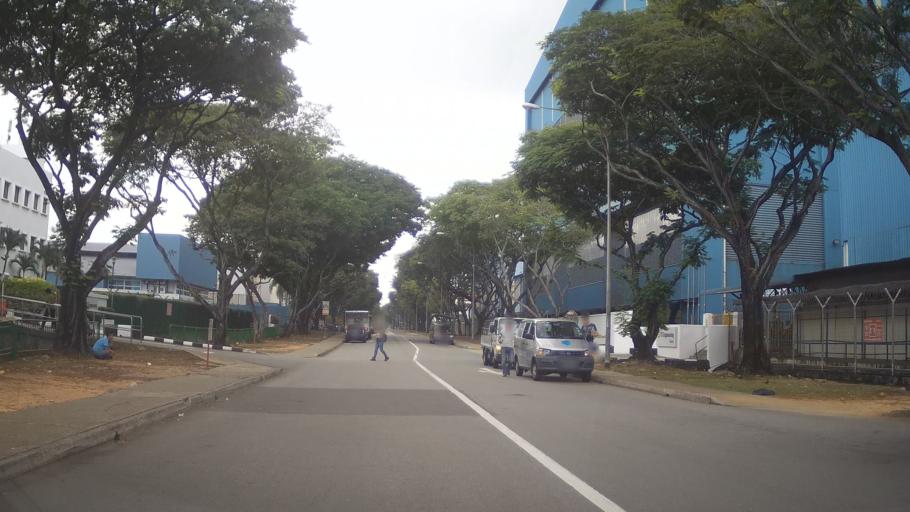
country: SG
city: Singapore
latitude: 1.3012
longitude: 103.6795
